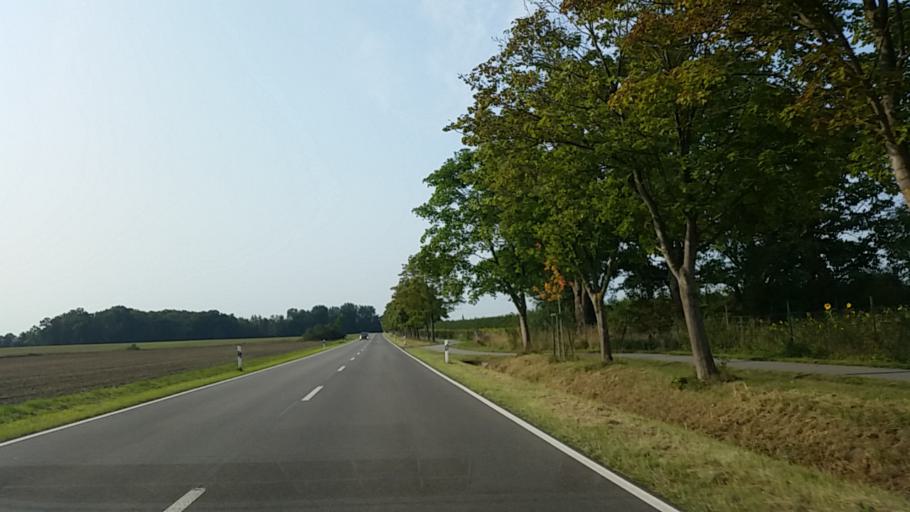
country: DE
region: Mecklenburg-Vorpommern
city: Lubtheen
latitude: 53.3888
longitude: 11.0886
